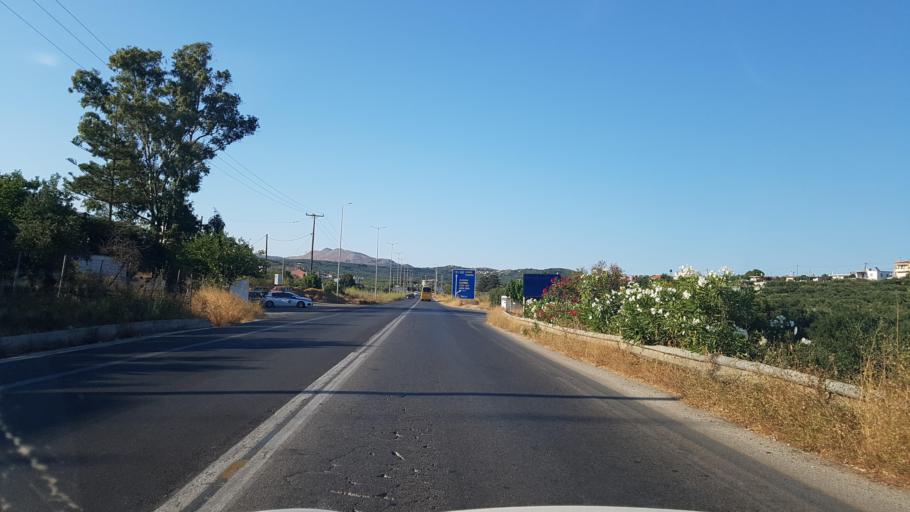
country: GR
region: Crete
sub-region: Nomos Chanias
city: Kolympari
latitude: 35.5231
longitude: 23.7471
